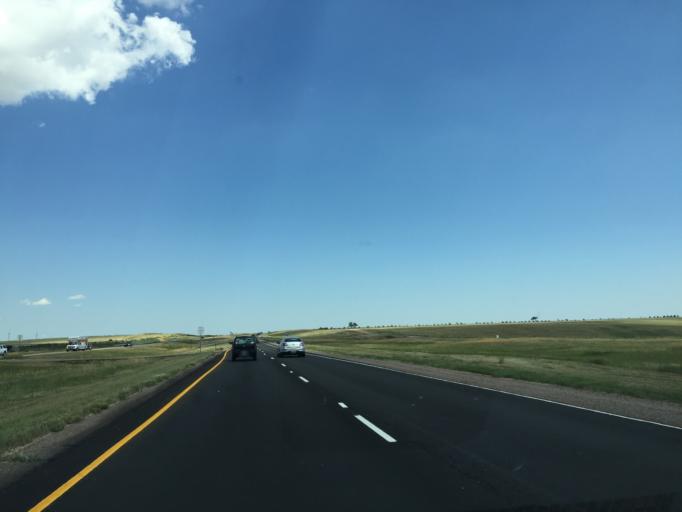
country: US
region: Colorado
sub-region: Lincoln County
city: Hugo
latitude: 39.2792
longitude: -103.3884
